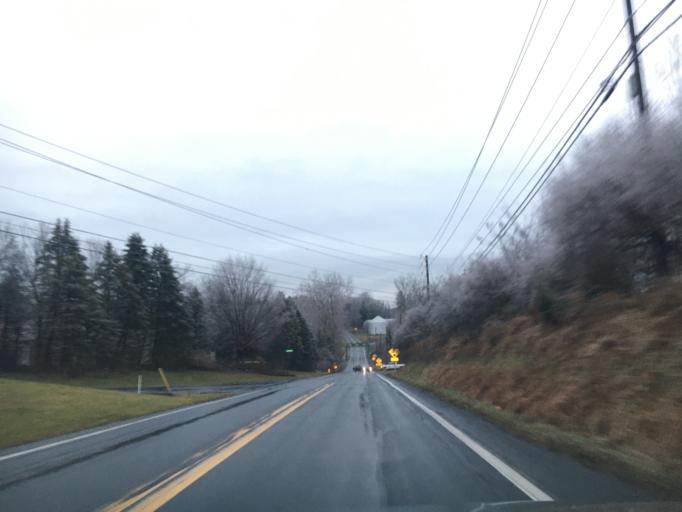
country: US
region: Pennsylvania
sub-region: Lehigh County
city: Schnecksville
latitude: 40.6338
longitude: -75.6050
